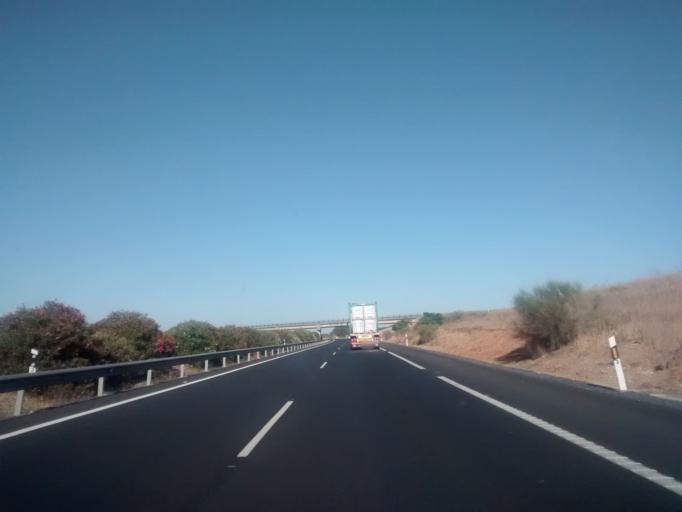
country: ES
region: Andalusia
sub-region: Provincia de Huelva
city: Lucena del Puerto
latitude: 37.3404
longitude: -6.7343
